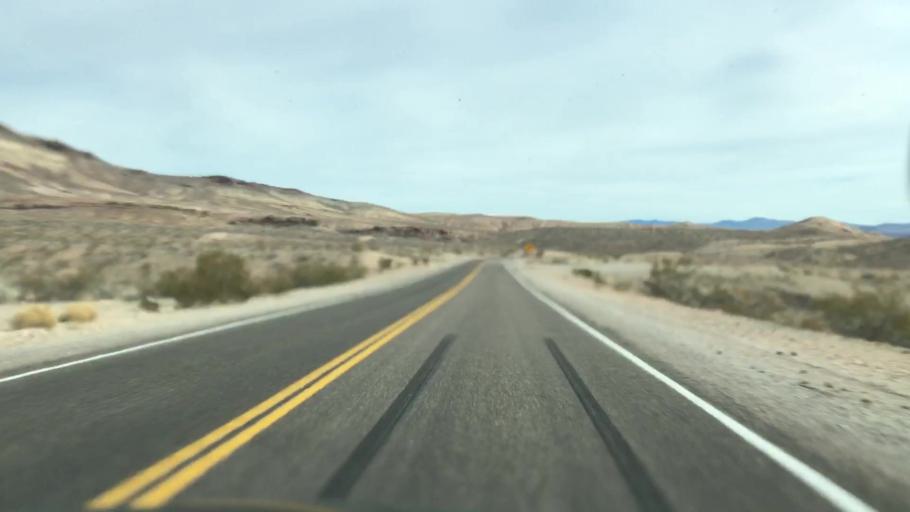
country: US
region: Nevada
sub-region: Nye County
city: Beatty
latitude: 36.9013
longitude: -116.7918
